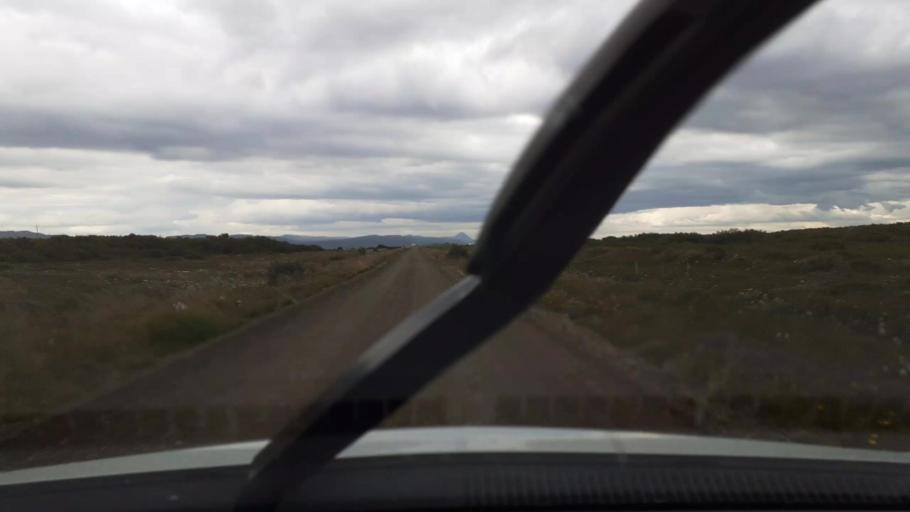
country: IS
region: West
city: Borgarnes
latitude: 64.6382
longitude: -21.9070
